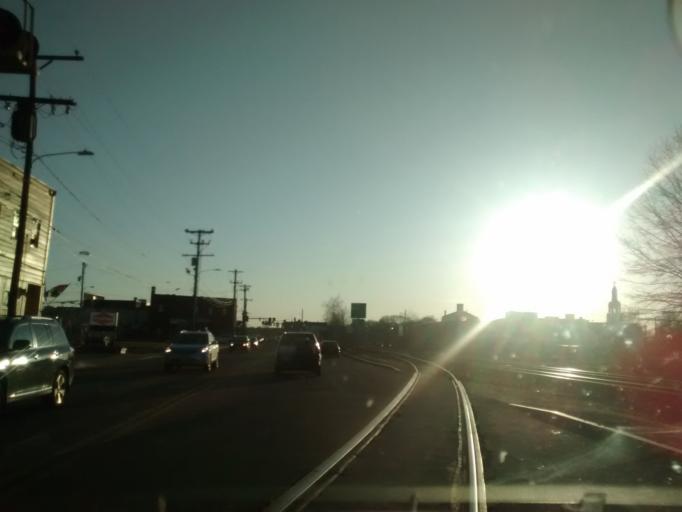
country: US
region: Massachusetts
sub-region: Middlesex County
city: Framingham
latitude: 42.2774
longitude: -71.4144
